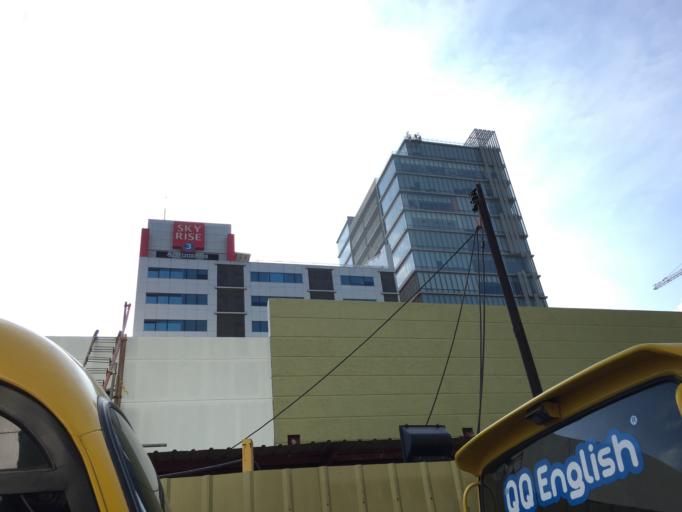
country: PH
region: Central Visayas
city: Mandaue City
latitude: 10.3297
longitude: 123.9065
